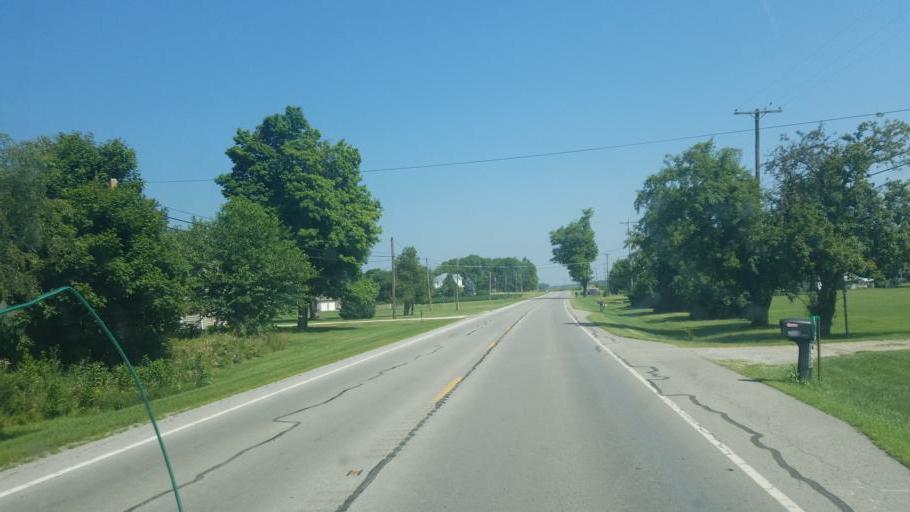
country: US
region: Ohio
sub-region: Hardin County
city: Kenton
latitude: 40.6709
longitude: -83.6115
